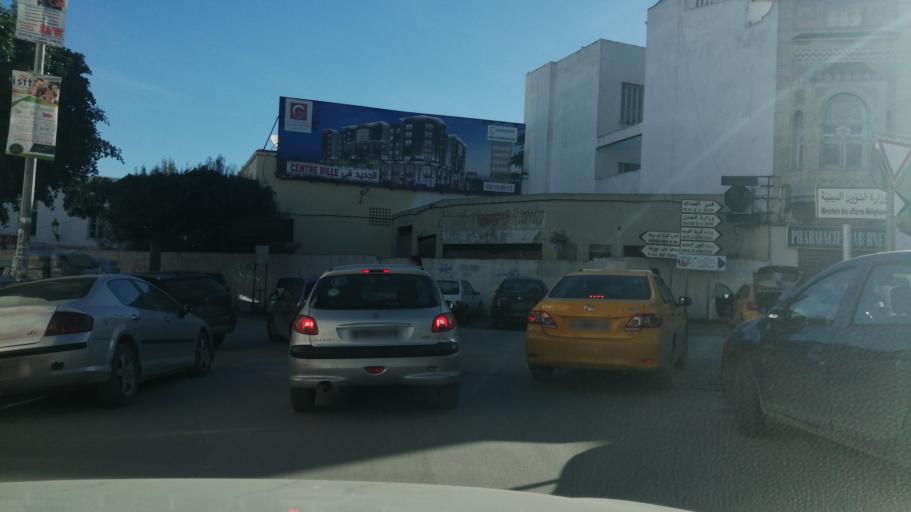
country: TN
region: Tunis
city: Tunis
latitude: 36.8030
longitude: 10.1653
